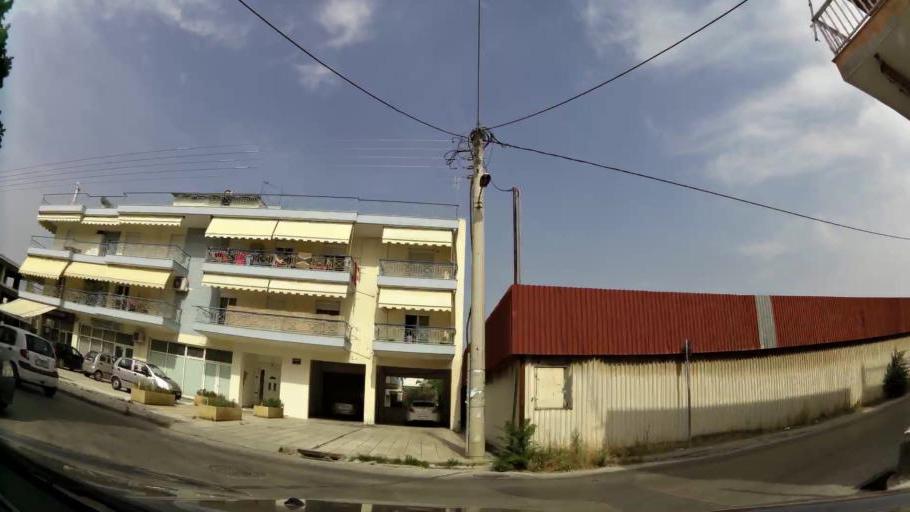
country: GR
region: Central Macedonia
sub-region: Nomos Thessalonikis
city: Stavroupoli
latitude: 40.6803
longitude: 22.9371
